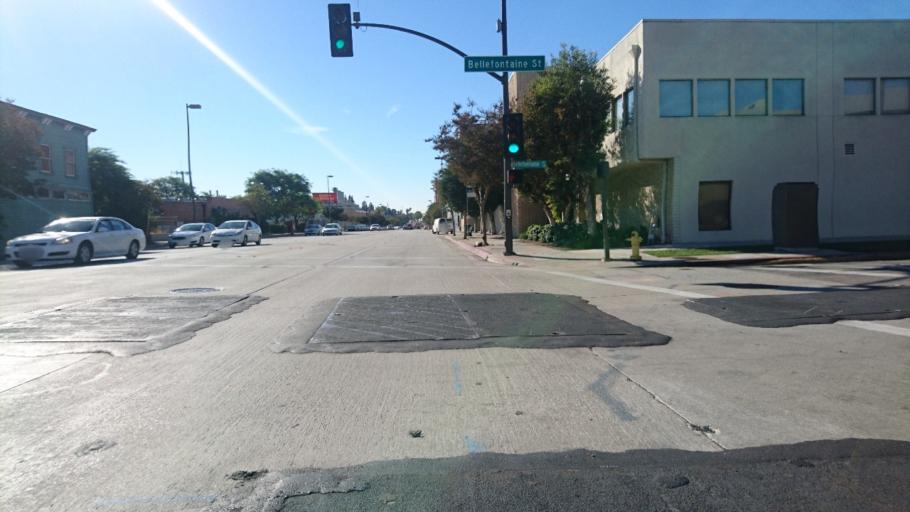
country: US
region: California
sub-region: Los Angeles County
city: South Pasadena
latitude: 34.1316
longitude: -118.1504
